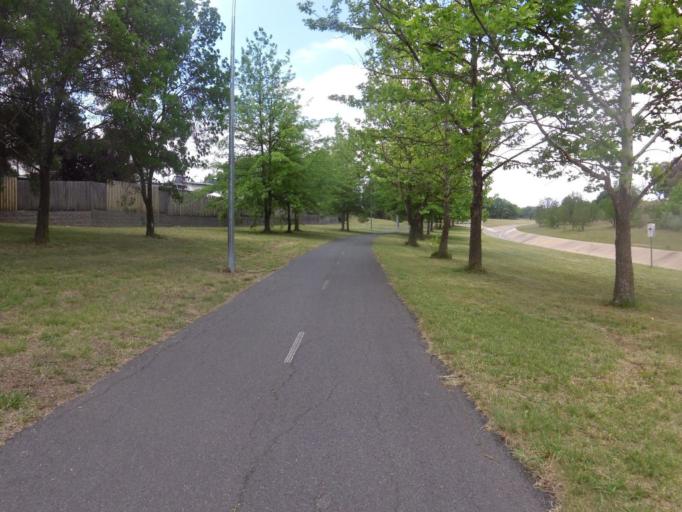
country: AU
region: Australian Capital Territory
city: Macarthur
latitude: -35.4192
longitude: 149.1062
